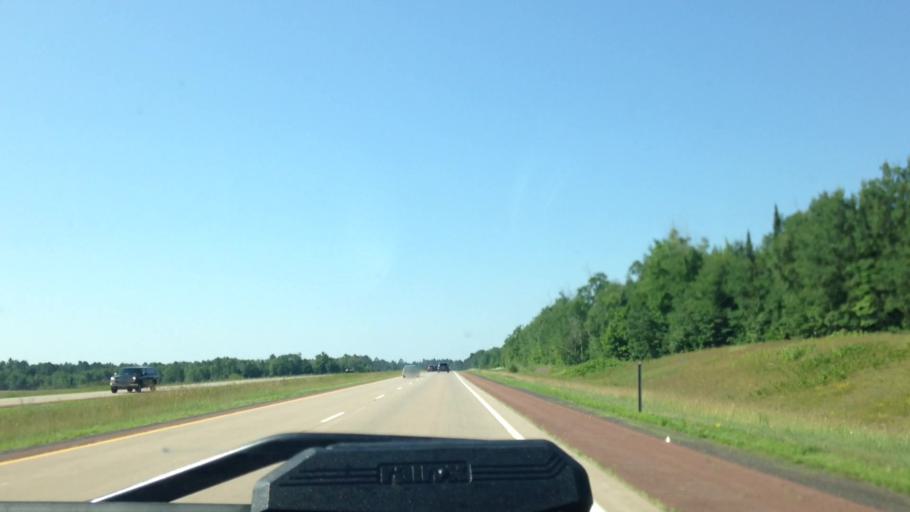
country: US
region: Wisconsin
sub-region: Douglas County
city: Lake Nebagamon
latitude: 46.3689
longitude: -91.8286
